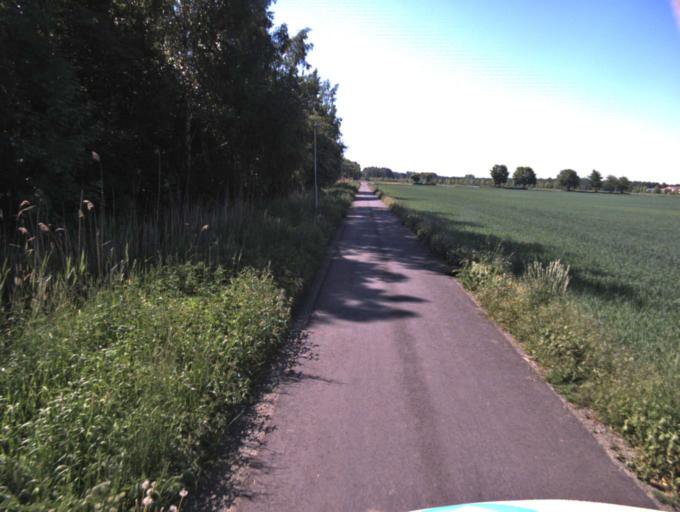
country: SE
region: Skane
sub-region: Kristianstads Kommun
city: Kristianstad
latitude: 56.0316
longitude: 14.1909
